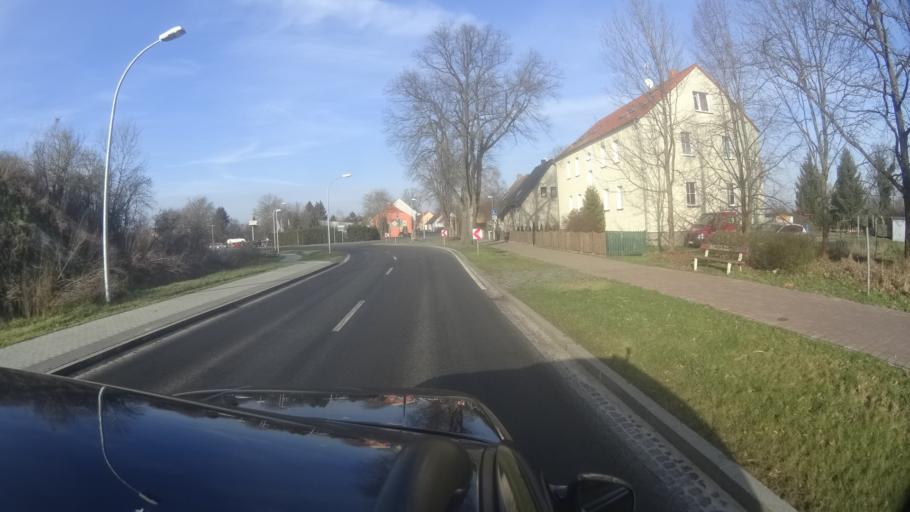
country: DE
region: Brandenburg
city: Kremmen
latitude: 52.7562
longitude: 13.0354
